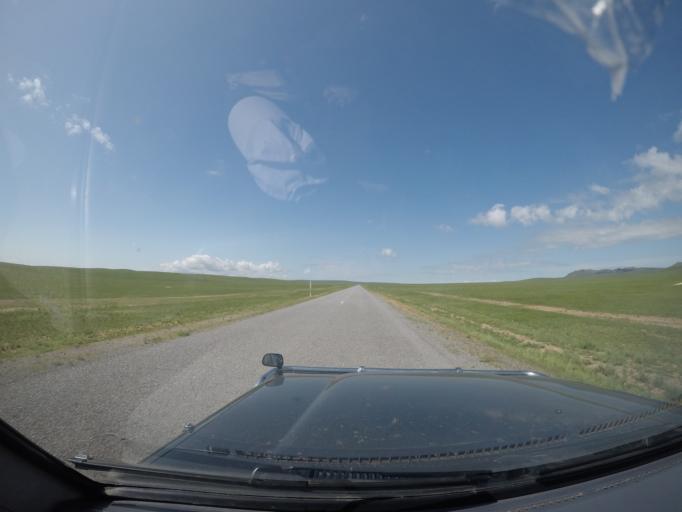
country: MN
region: Hentiy
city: Bayan
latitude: 47.3173
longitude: 111.3790
